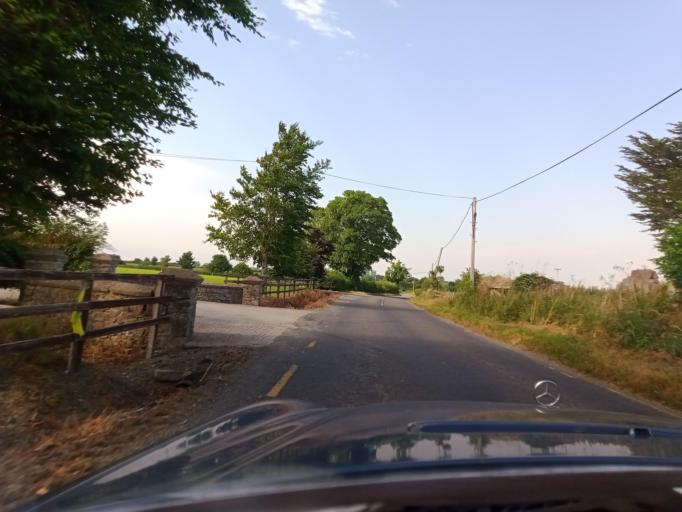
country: IE
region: Leinster
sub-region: Kilkenny
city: Callan
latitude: 52.5248
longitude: -7.3007
